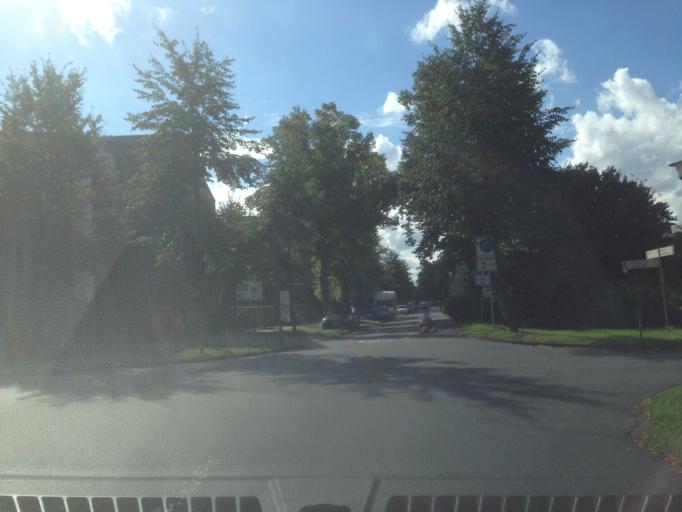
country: DE
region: North Rhine-Westphalia
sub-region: Regierungsbezirk Munster
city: Muenster
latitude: 51.9600
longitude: 7.5889
